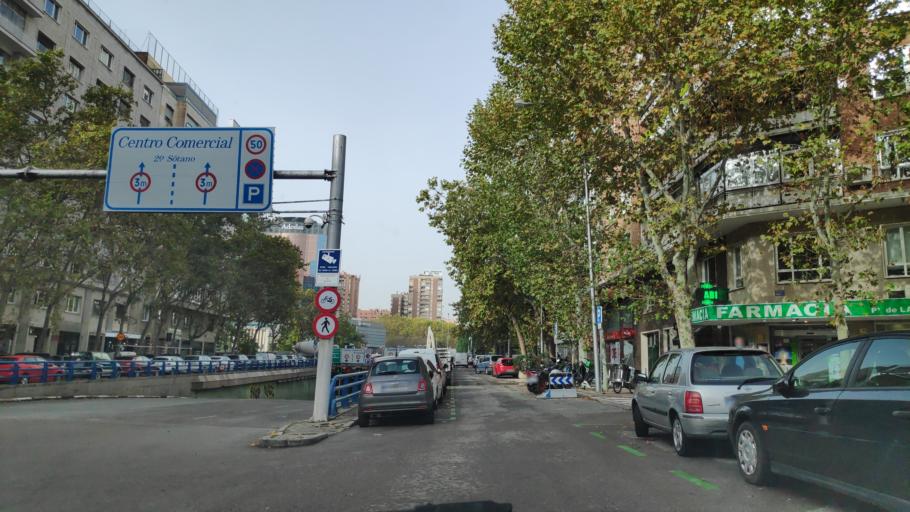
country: ES
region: Madrid
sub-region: Provincia de Madrid
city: Chamartin
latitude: 40.4491
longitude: -3.6892
